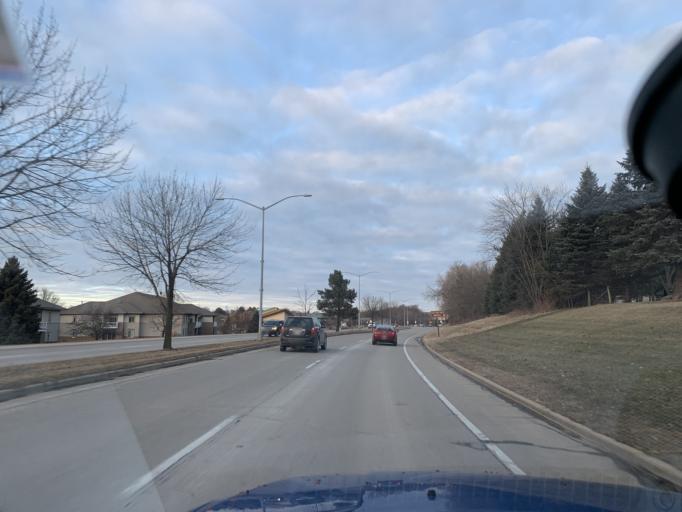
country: US
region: Wisconsin
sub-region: Dane County
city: Fitchburg
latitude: 43.0113
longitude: -89.4283
